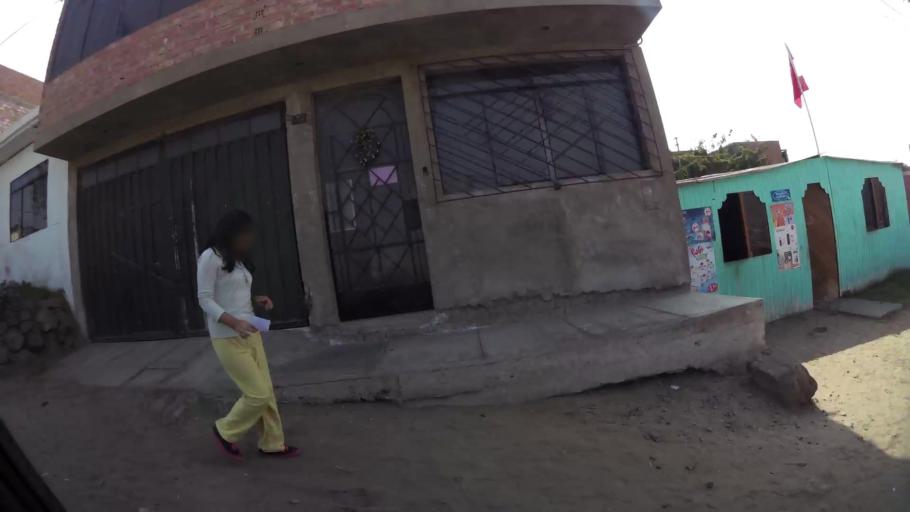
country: PE
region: Lima
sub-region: Lima
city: Santa Rosa
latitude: -11.7845
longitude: -77.1635
